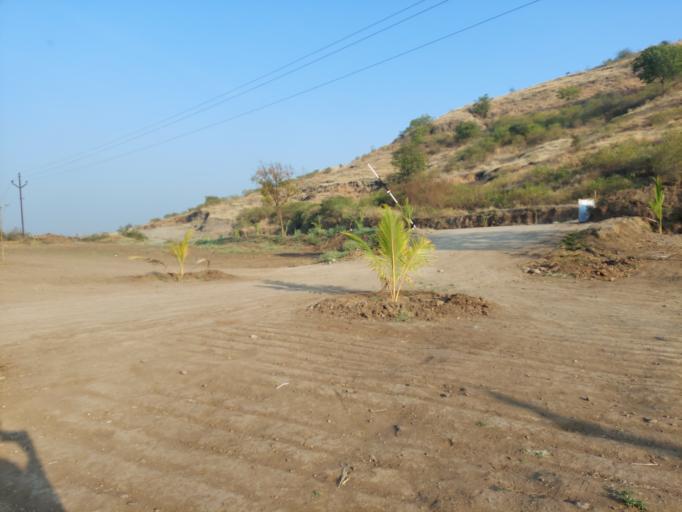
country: IN
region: Maharashtra
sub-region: Pune Division
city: Sasvad
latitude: 18.4209
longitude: 73.9983
